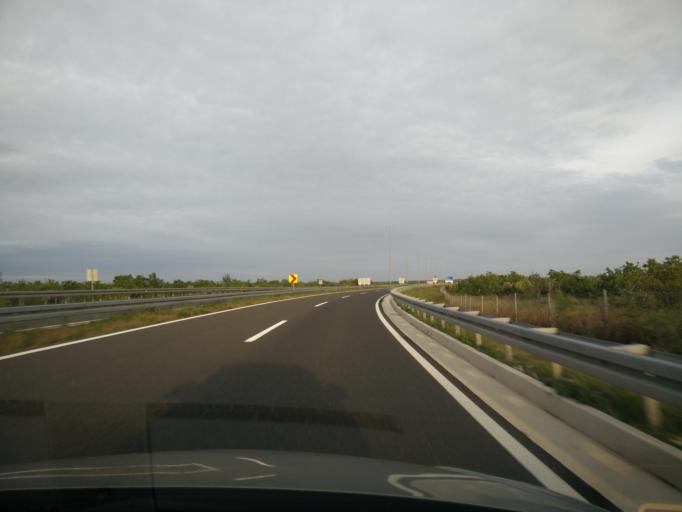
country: HR
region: Zadarska
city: Galovac
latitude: 44.1183
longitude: 15.4291
